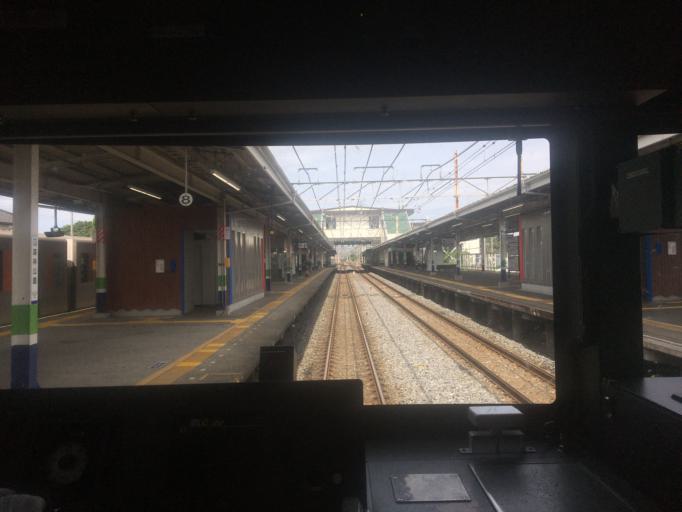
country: JP
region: Saitama
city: Sakado
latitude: 36.0450
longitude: 139.3762
